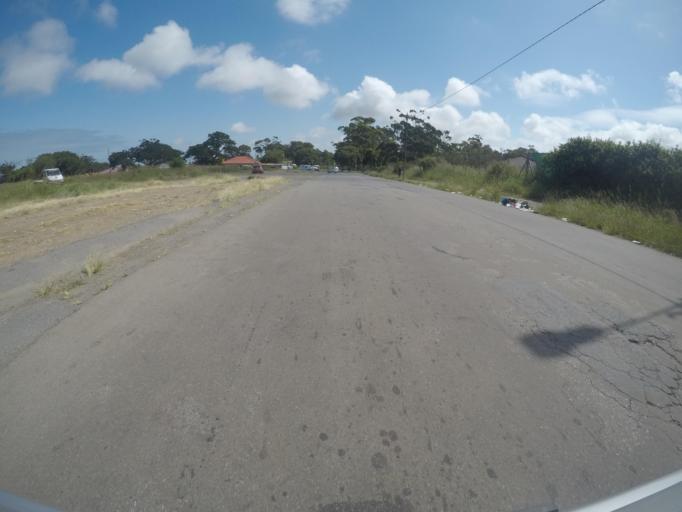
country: ZA
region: Eastern Cape
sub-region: Buffalo City Metropolitan Municipality
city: East London
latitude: -32.9978
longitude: 27.8929
